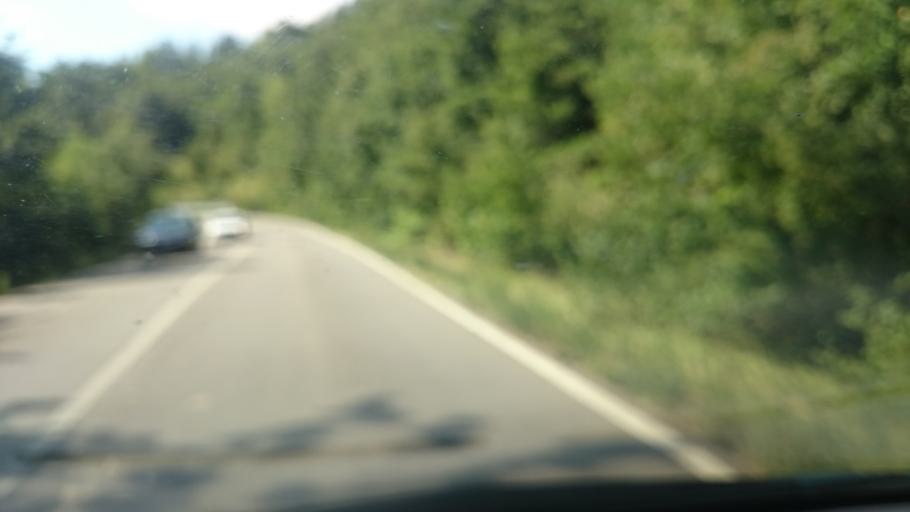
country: IT
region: Emilia-Romagna
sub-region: Provincia di Reggio Emilia
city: Toano
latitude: 44.4115
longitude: 10.5966
